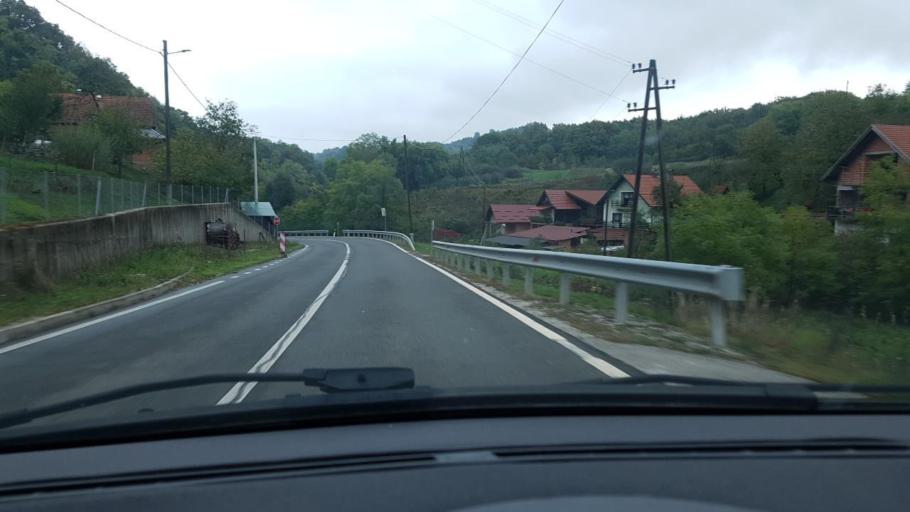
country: HR
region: Krapinsko-Zagorska
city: Marija Bistrica
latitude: 45.9806
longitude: 16.1087
